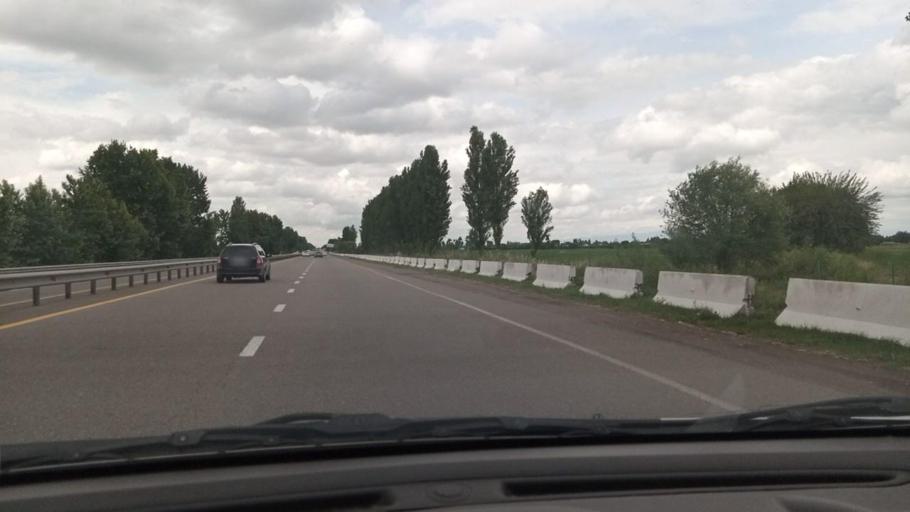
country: UZ
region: Toshkent Shahri
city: Bektemir
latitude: 41.2102
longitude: 69.4028
